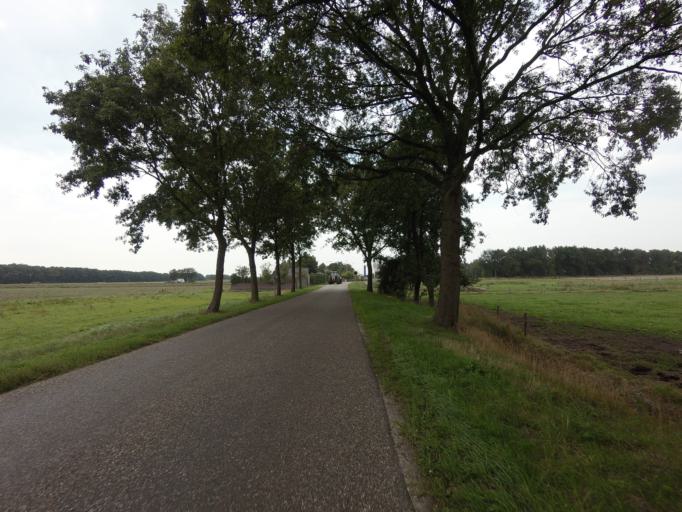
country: NL
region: Drenthe
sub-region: Gemeente Tynaarlo
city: Tynaarlo
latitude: 53.0364
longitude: 6.6087
